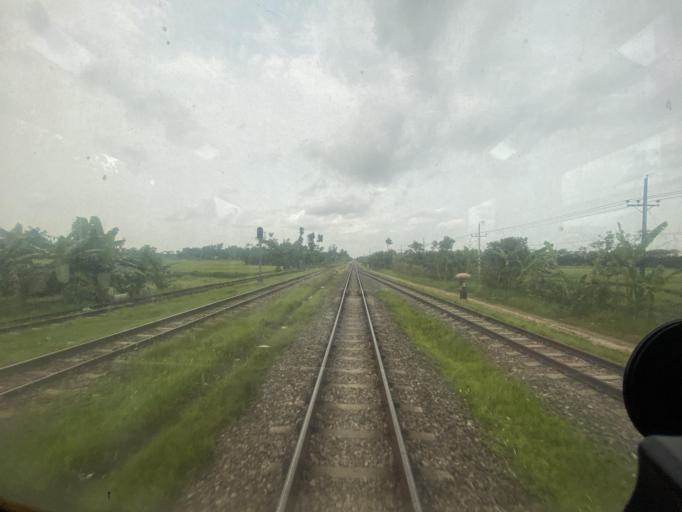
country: BD
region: Chittagong
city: Laksham
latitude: 23.2030
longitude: 91.1568
